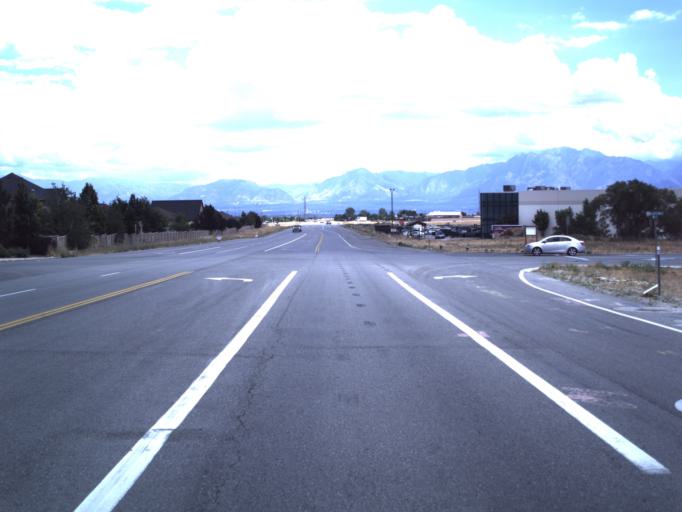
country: US
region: Utah
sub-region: Salt Lake County
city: Oquirrh
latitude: 40.5845
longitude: -112.0435
